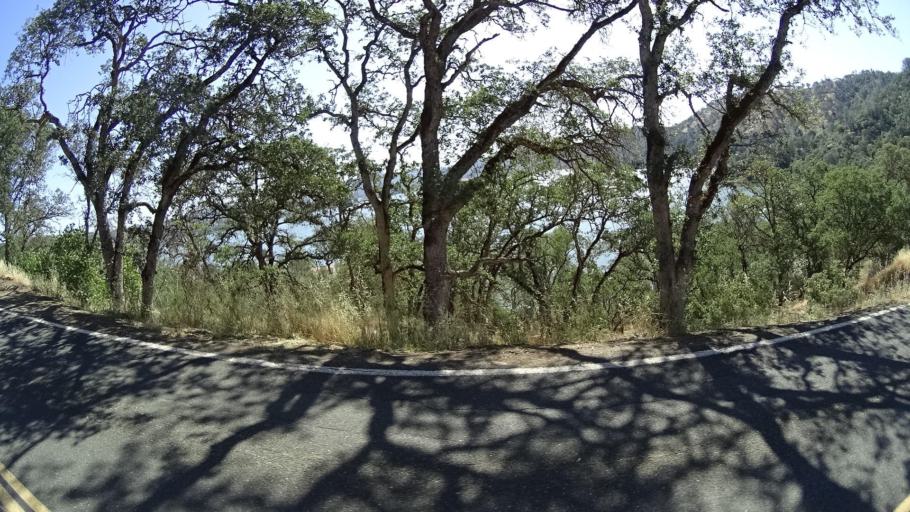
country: US
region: California
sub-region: Lake County
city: Clearlake Oaks
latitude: 39.0014
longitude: -122.7016
